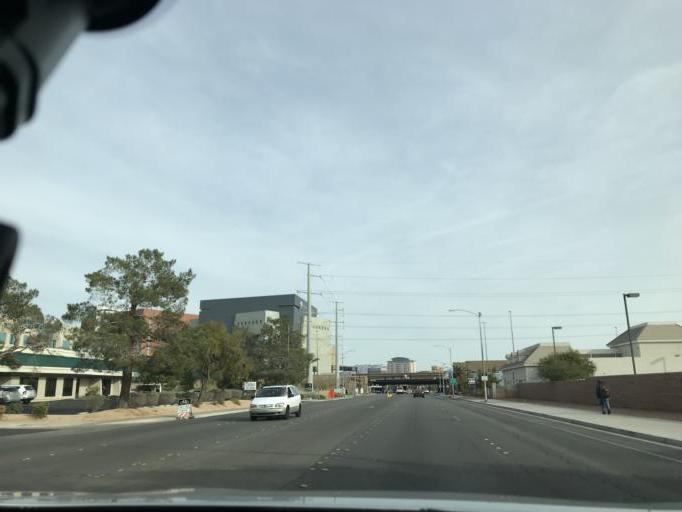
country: US
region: Nevada
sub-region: Clark County
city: Las Vegas
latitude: 36.1662
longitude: -115.1638
